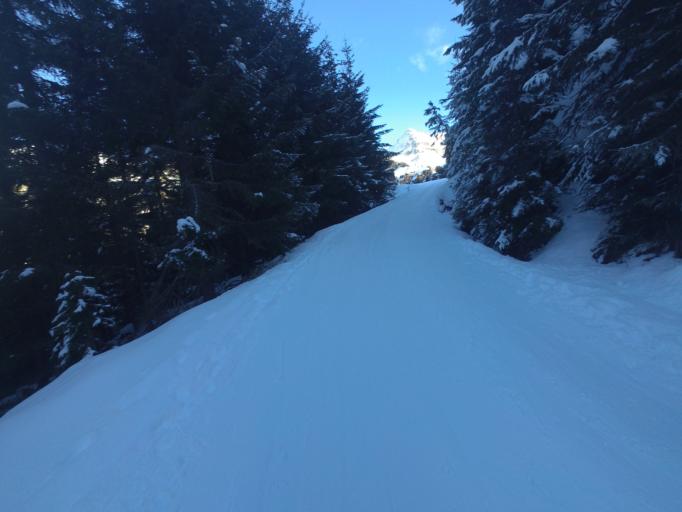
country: AT
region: Salzburg
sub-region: Politischer Bezirk Sankt Johann im Pongau
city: Huttschlag
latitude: 47.1788
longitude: 13.2734
